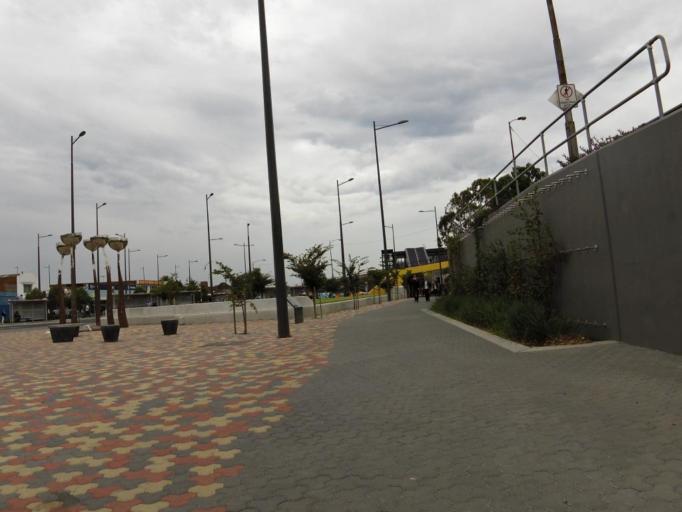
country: AU
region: Victoria
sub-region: Brimbank
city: Sunshine West
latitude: -37.7867
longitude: 144.8321
